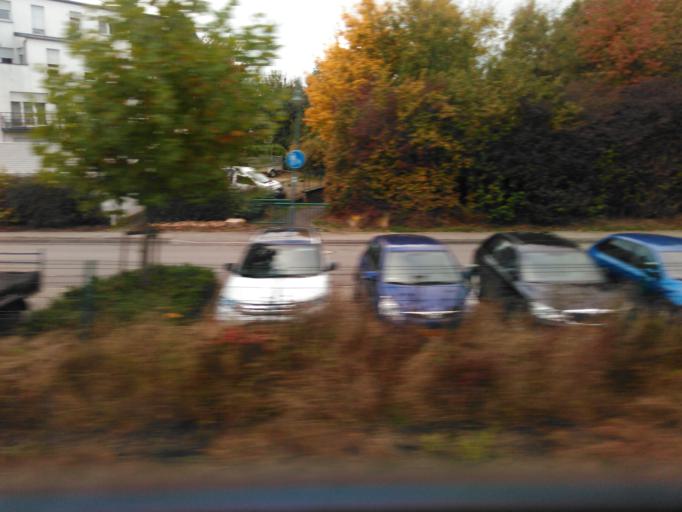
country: LU
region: Luxembourg
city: Crauthem
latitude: 49.5403
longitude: 6.1319
